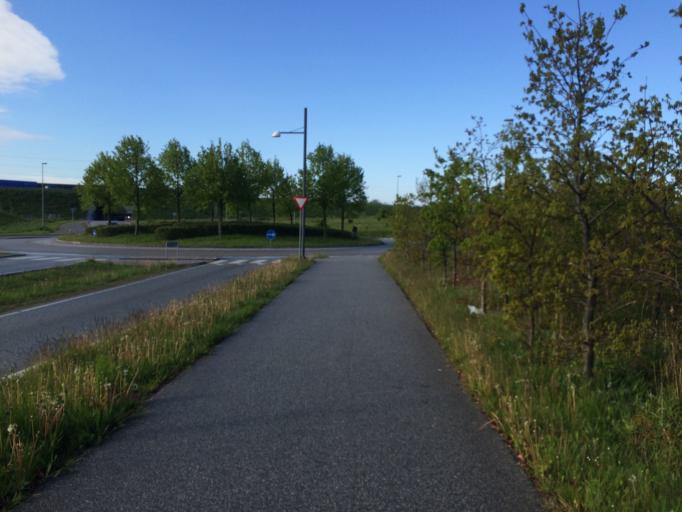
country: DK
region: Zealand
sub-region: Roskilde Kommune
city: Vindinge
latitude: 55.6511
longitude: 12.1442
